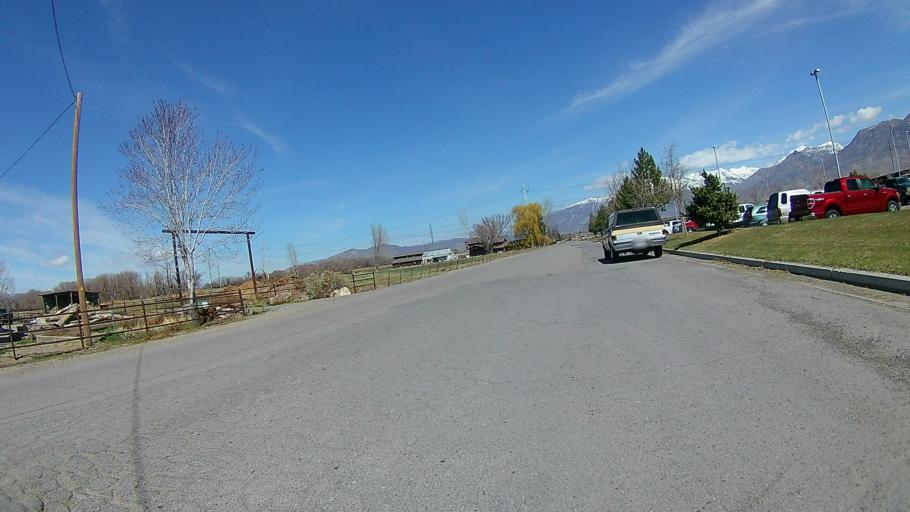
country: US
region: Utah
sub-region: Utah County
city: American Fork
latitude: 40.3479
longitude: -111.7952
